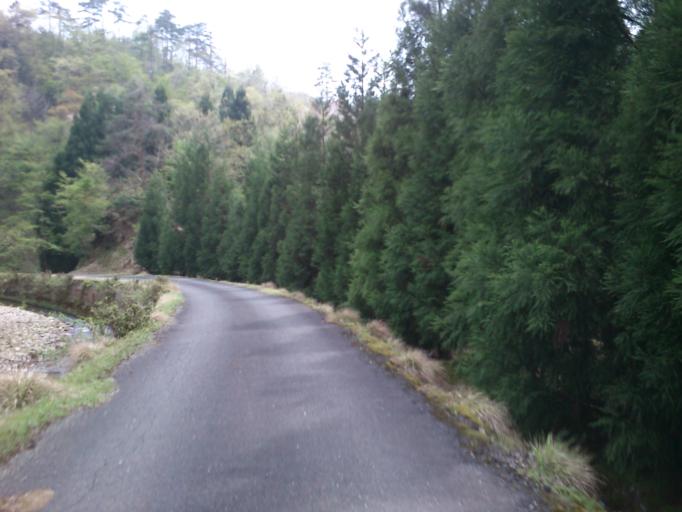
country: JP
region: Kyoto
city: Maizuru
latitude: 35.4035
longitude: 135.5050
